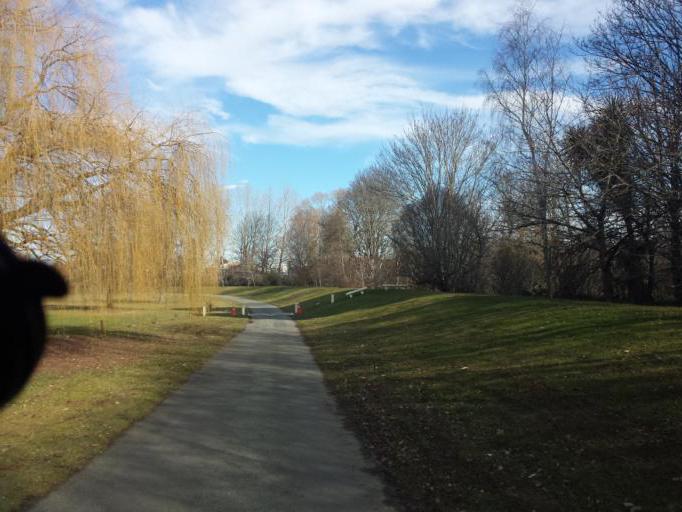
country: NZ
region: Canterbury
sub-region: Timaru District
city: Pleasant Point
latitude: -44.0883
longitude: 171.2447
